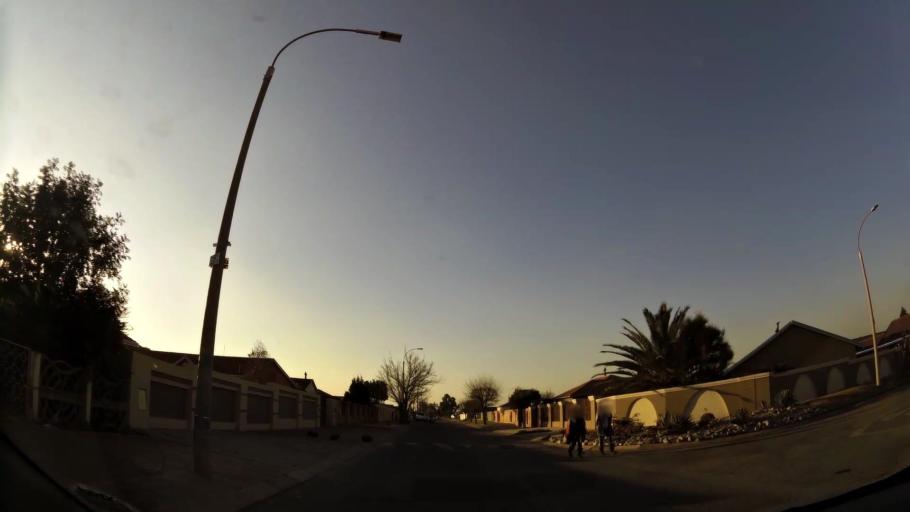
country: ZA
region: Gauteng
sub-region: West Rand District Municipality
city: Randfontein
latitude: -26.2049
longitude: 27.6520
